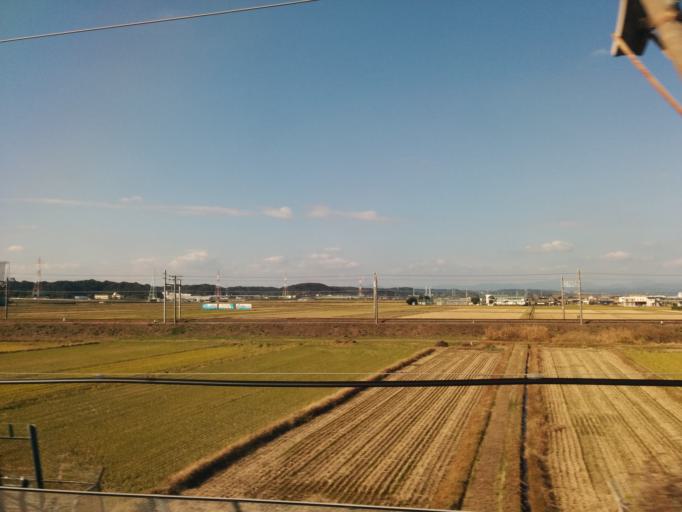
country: JP
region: Shizuoka
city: Fukuroi
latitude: 34.7284
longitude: 137.9021
